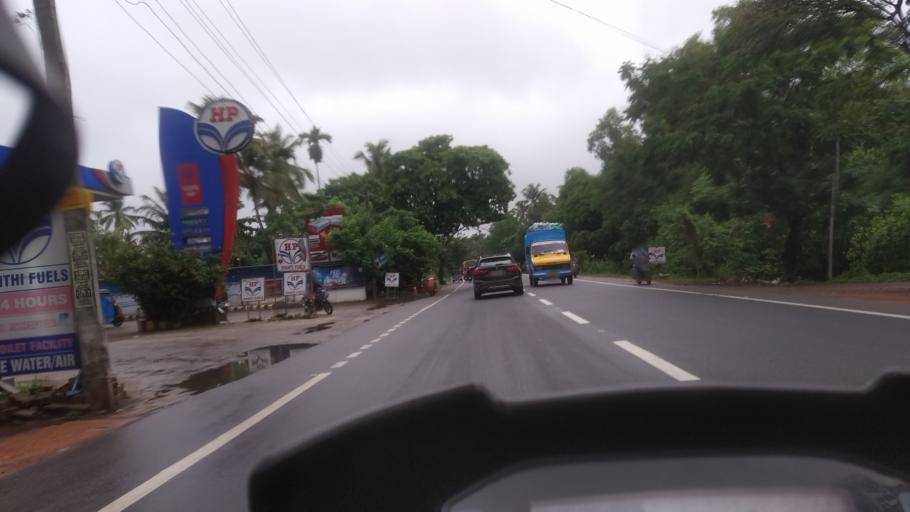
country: IN
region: Kerala
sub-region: Alappuzha
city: Mavelikara
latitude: 9.2972
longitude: 76.4340
